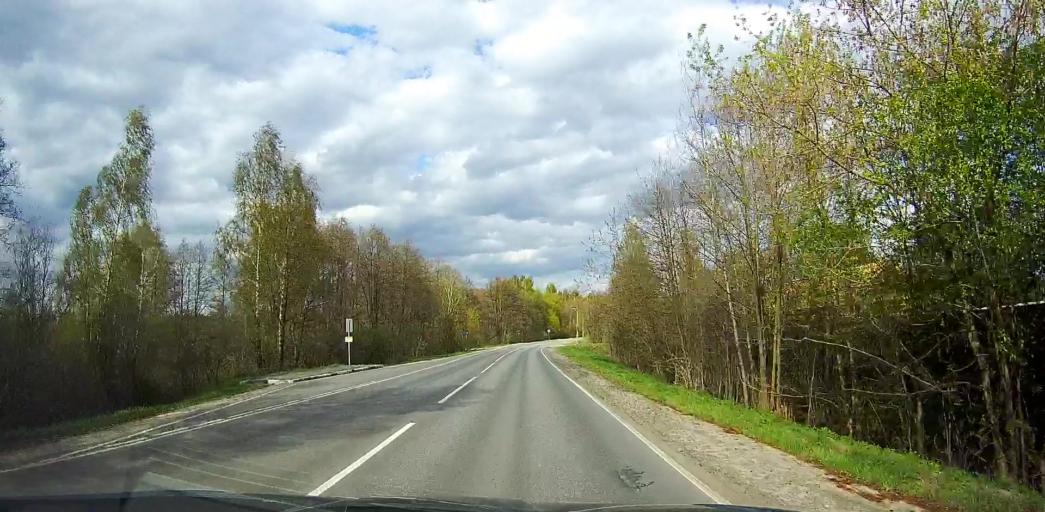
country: RU
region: Moskovskaya
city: Rakhmanovo
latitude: 55.7340
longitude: 38.6336
